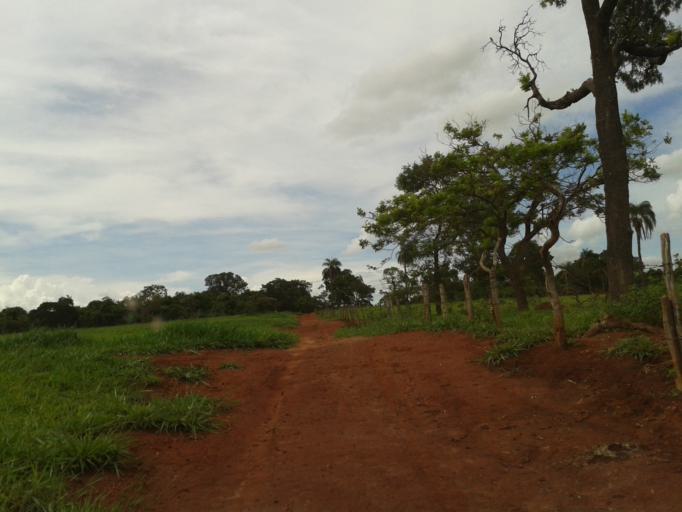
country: BR
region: Minas Gerais
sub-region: Santa Vitoria
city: Santa Vitoria
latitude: -18.7983
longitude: -49.8508
